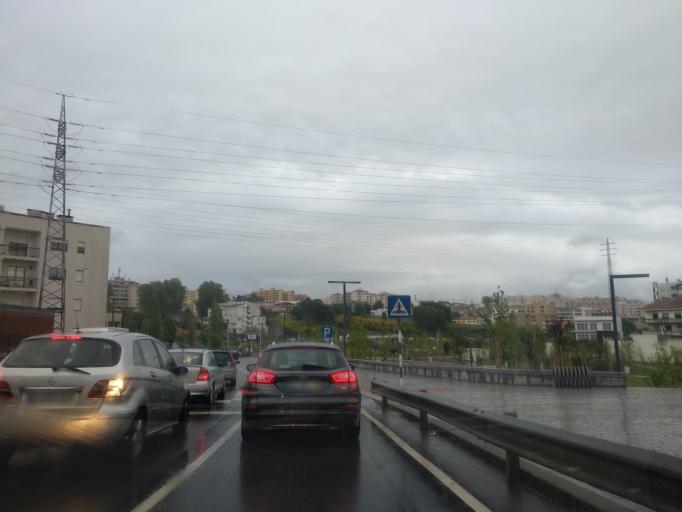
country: PT
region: Porto
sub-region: Gondomar
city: Rio Tinto
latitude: 41.1782
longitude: -8.5636
